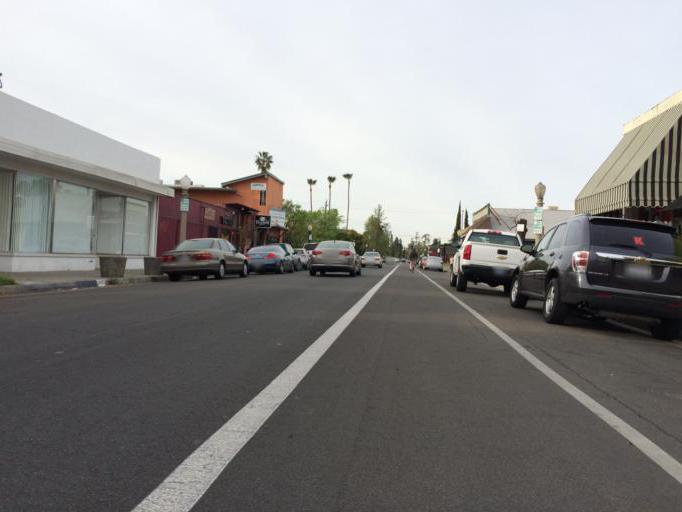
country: US
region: California
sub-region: Fresno County
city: Fresno
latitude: 36.7620
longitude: -119.7990
